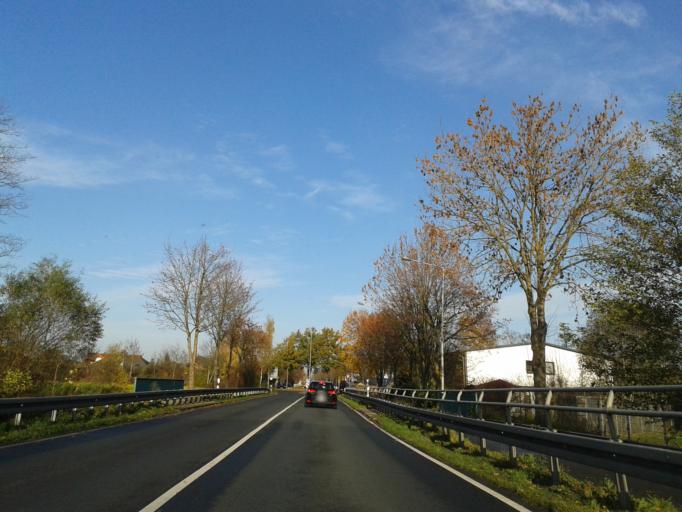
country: DE
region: North Rhine-Westphalia
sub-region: Regierungsbezirk Detmold
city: Hovelhof
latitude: 51.8140
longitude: 8.6650
